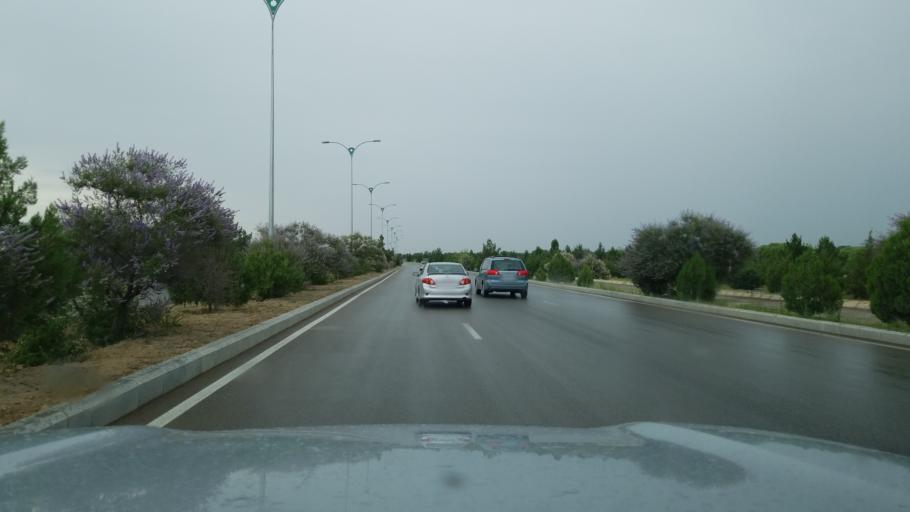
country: TM
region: Ahal
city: Abadan
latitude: 37.9725
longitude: 58.2386
